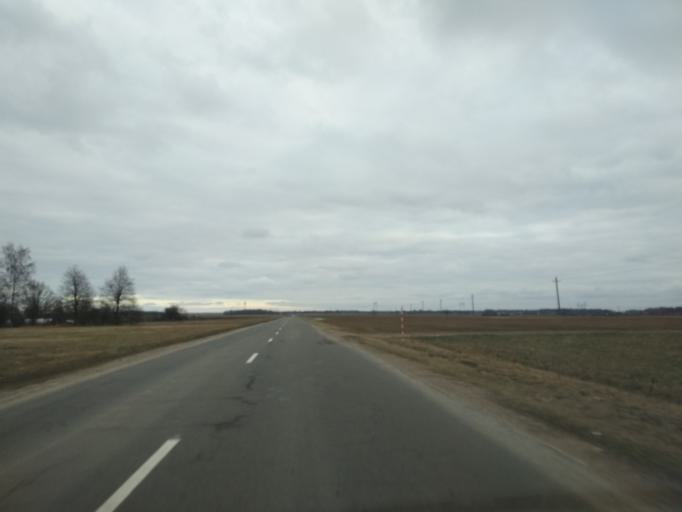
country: BY
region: Minsk
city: Mar''ina Horka
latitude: 53.5627
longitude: 28.0339
